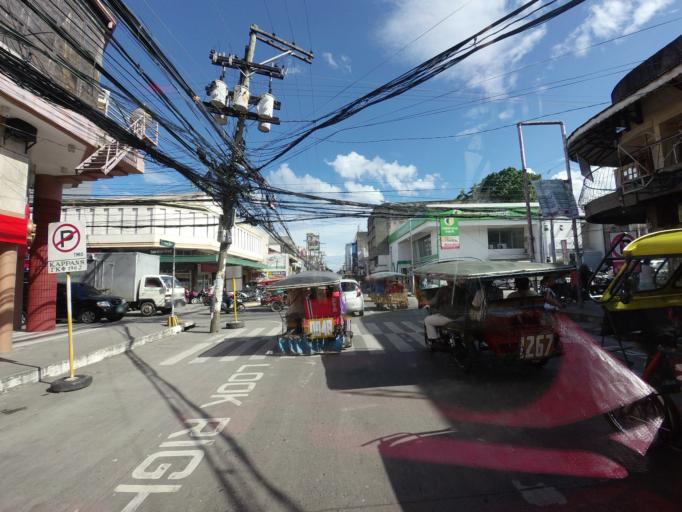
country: PH
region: Central Visayas
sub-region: Province of Negros Oriental
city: Dumaguete
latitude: 9.3076
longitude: 123.3083
